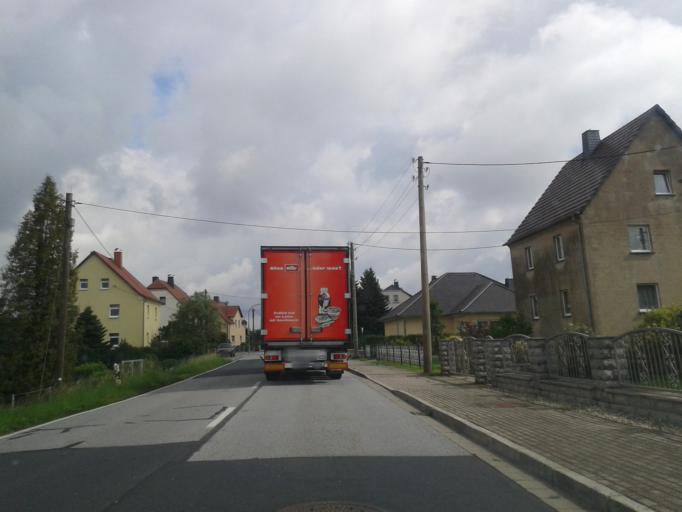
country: DE
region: Saxony
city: Lichtenberg
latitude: 51.1505
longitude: 13.9622
